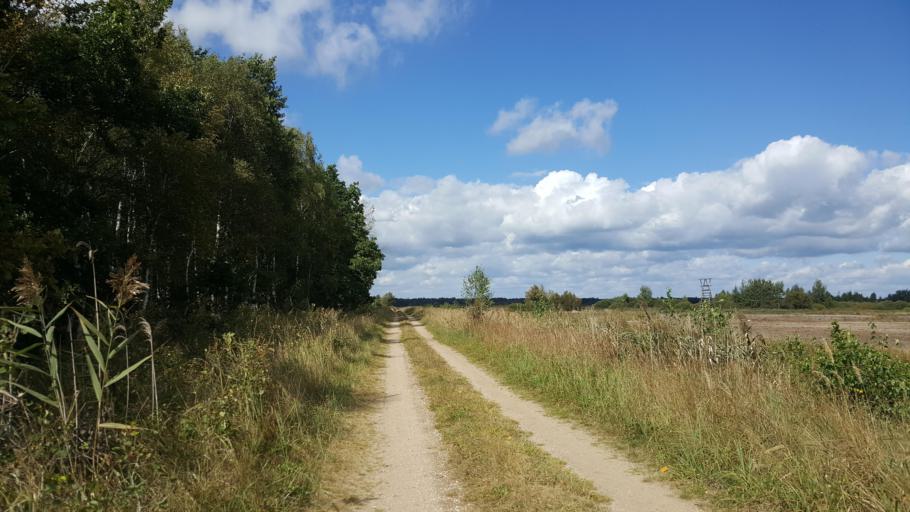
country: BY
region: Brest
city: Kamyanyets
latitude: 52.4585
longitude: 23.9311
